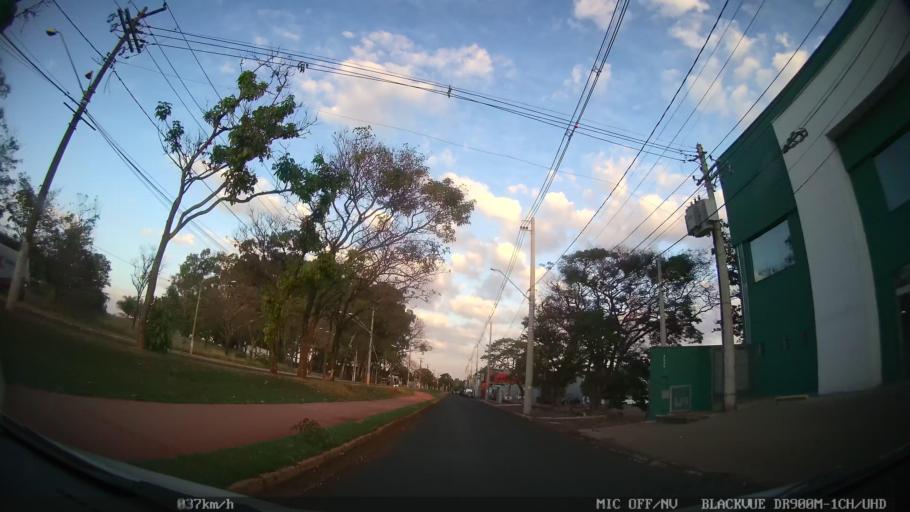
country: BR
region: Sao Paulo
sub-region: Ribeirao Preto
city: Ribeirao Preto
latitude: -21.1497
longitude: -47.7848
